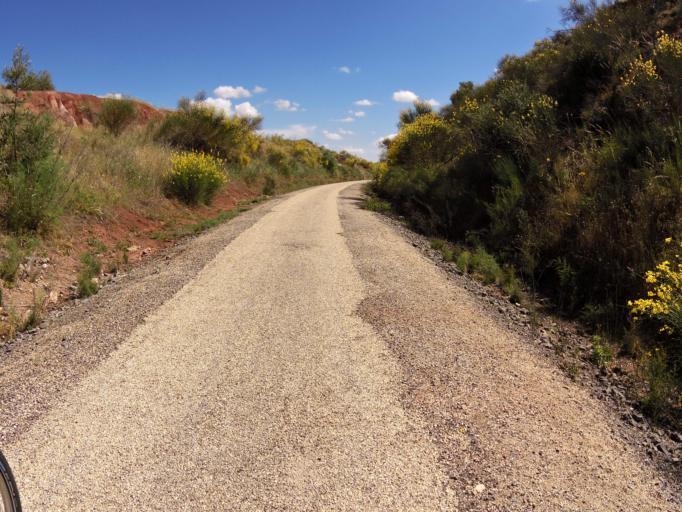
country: ES
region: Andalusia
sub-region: Provincia de Jaen
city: Alcaudete
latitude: 37.6181
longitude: -4.1086
